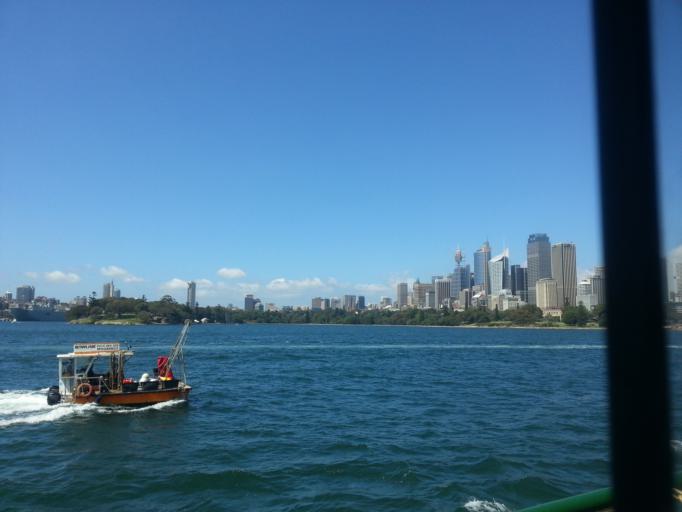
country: AU
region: New South Wales
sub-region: North Sydney
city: Kirribilli
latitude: -33.8535
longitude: 151.2221
